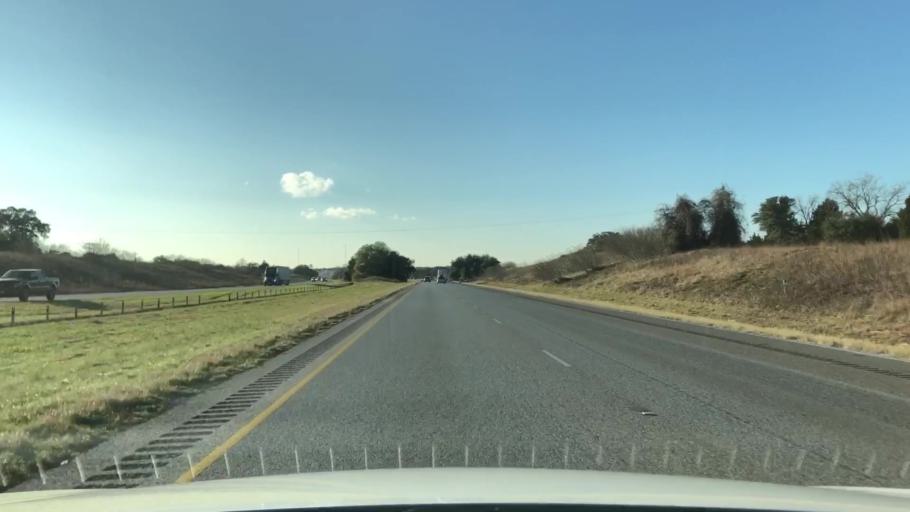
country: US
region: Texas
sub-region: Fayette County
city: Flatonia
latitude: 29.6964
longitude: -97.0347
